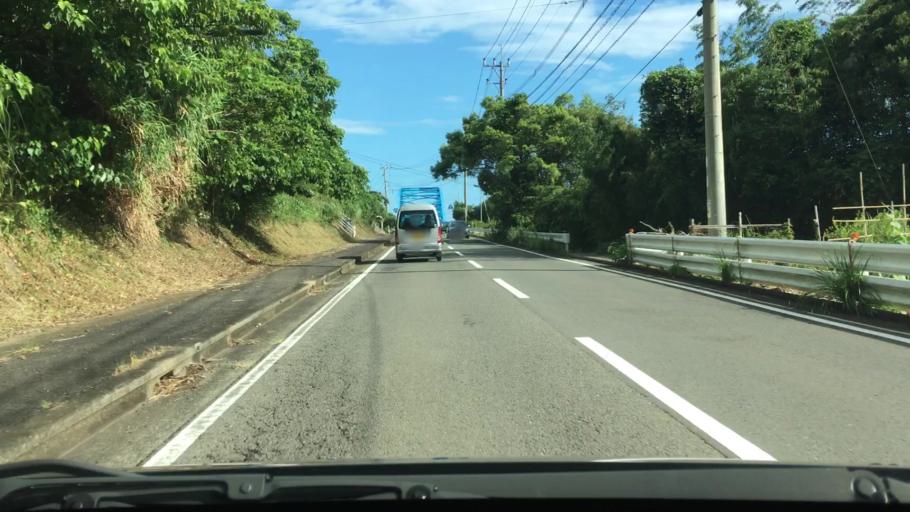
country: JP
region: Nagasaki
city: Togitsu
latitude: 32.8532
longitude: 129.6894
